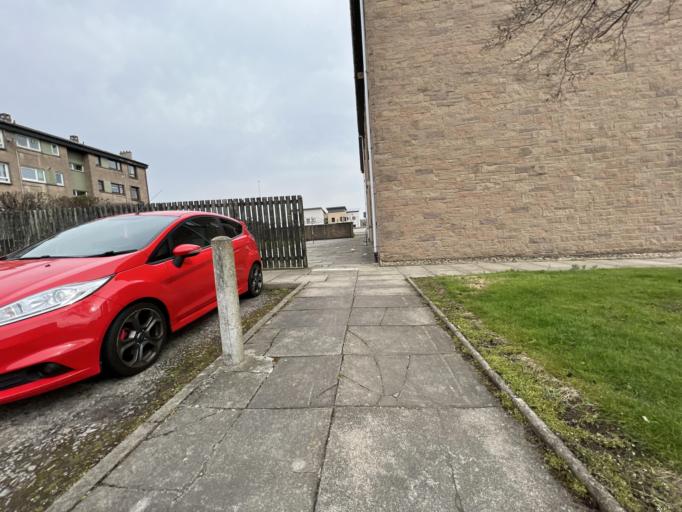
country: GB
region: Scotland
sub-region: Aberdeen City
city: Aberdeen
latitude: 57.1716
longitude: -2.1111
